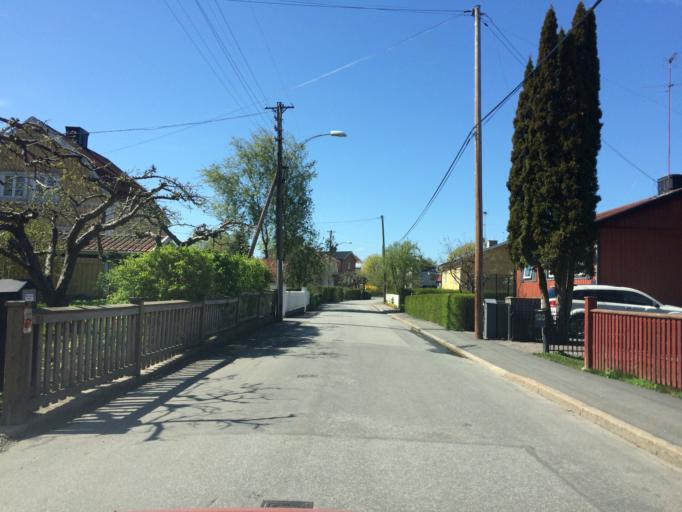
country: SE
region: Stockholm
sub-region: Huddinge Kommun
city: Segeltorp
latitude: 59.2912
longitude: 17.9573
